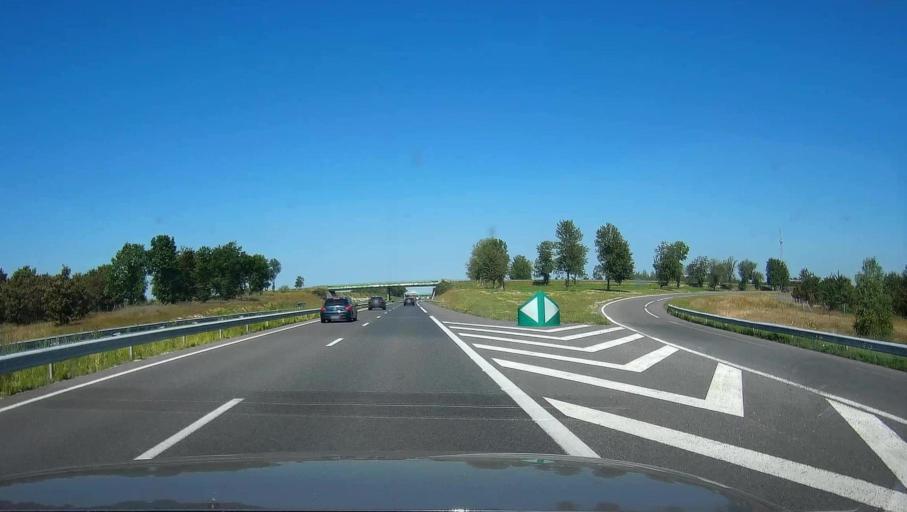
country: FR
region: Champagne-Ardenne
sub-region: Departement de la Marne
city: Fagnieres
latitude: 48.9052
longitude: 4.2847
